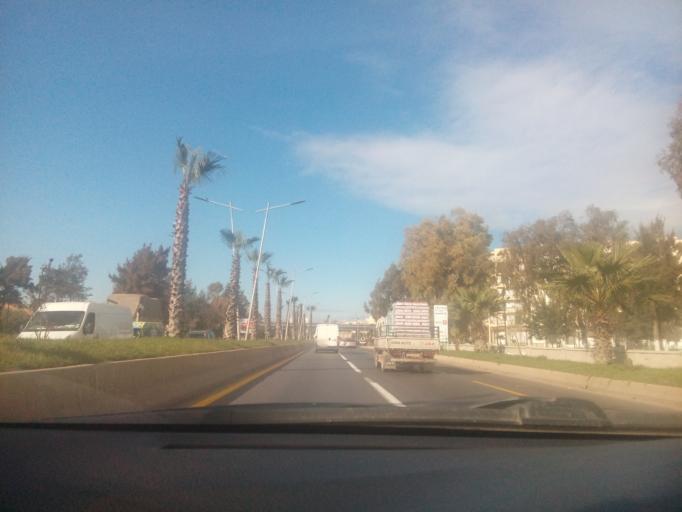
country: DZ
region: Oran
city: Oran
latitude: 35.6825
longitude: -0.6078
